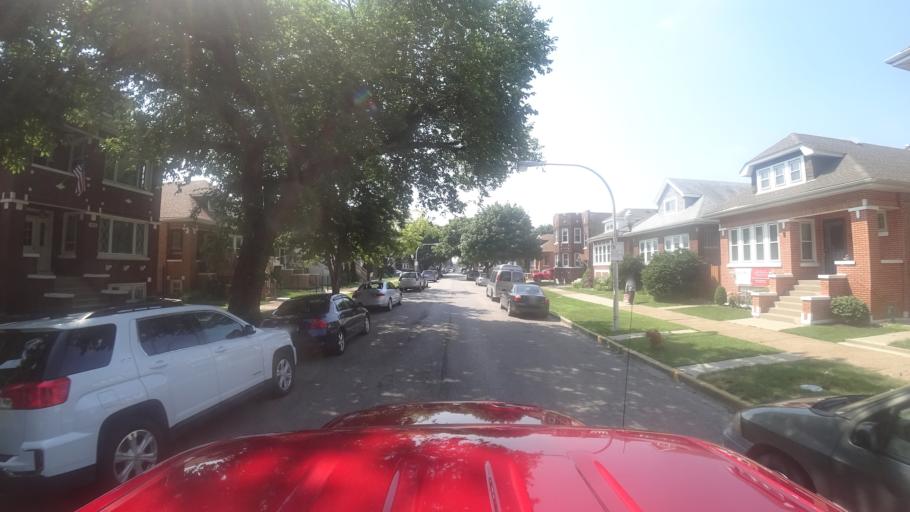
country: US
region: Illinois
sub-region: Cook County
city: Cicero
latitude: 41.8034
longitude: -87.7259
